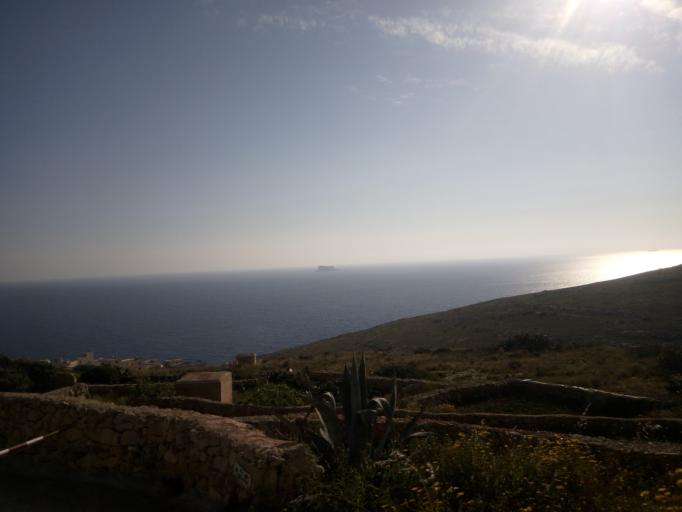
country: MT
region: Il-Qrendi
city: Qrendi
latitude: 35.8228
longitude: 14.4543
